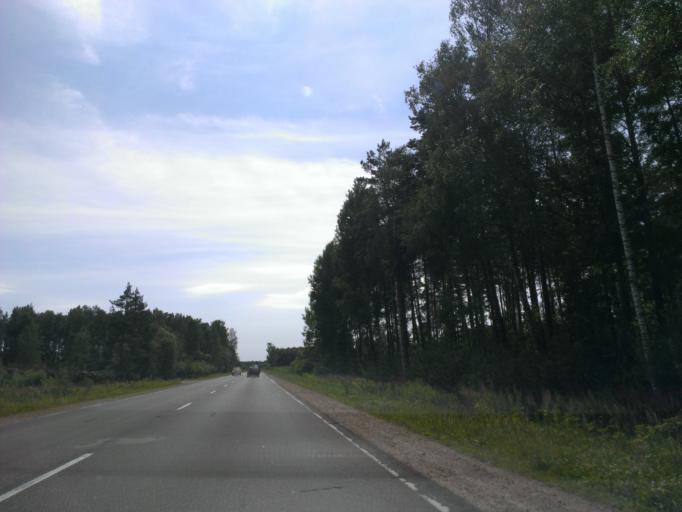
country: LV
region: Salaspils
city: Salaspils
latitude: 56.8915
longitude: 24.4071
